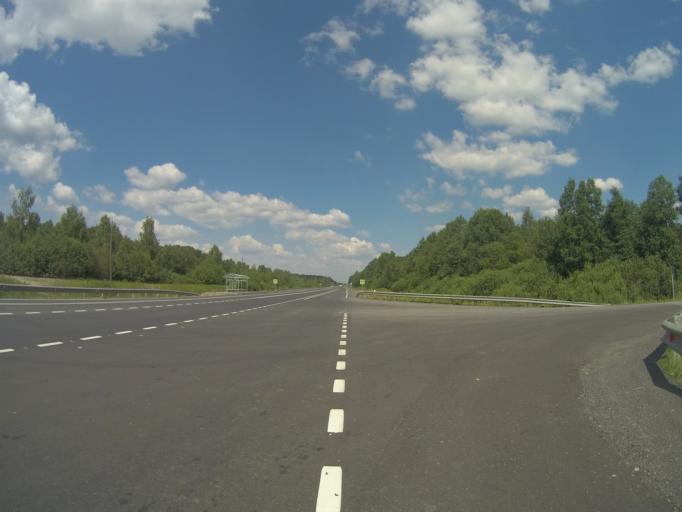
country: RU
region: Kostroma
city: Volgorechensk
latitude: 57.4016
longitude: 41.2085
